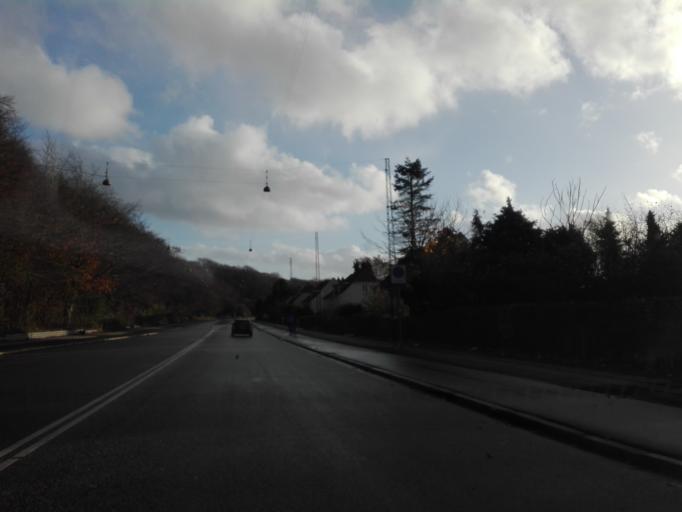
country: DK
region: Central Jutland
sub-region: Arhus Kommune
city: Arhus
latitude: 56.1770
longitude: 10.2196
